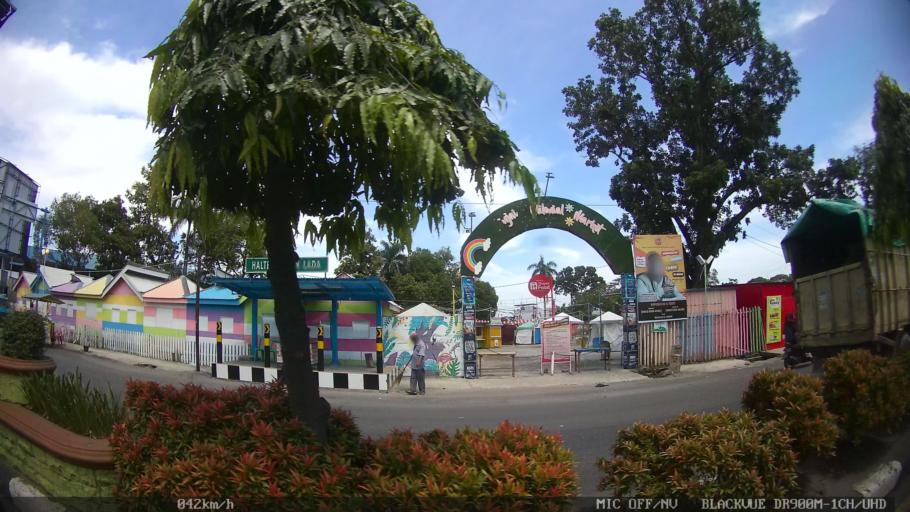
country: ID
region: North Sumatra
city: Binjai
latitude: 3.6164
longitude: 98.4979
